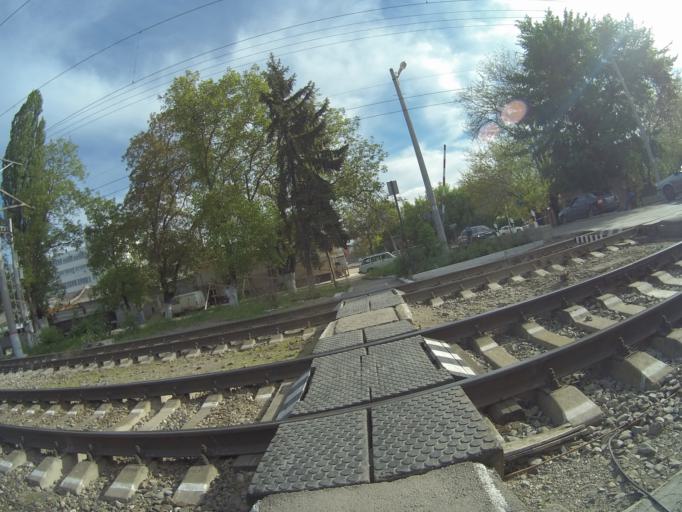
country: RU
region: Stavropol'skiy
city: Svobody
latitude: 44.0397
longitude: 43.0350
